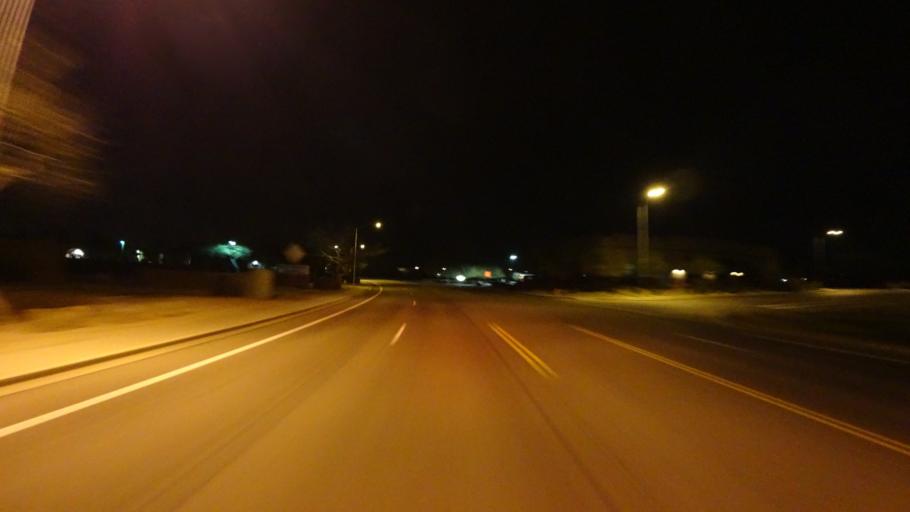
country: US
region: Arizona
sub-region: Maricopa County
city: Gilbert
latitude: 33.4112
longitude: -111.6944
